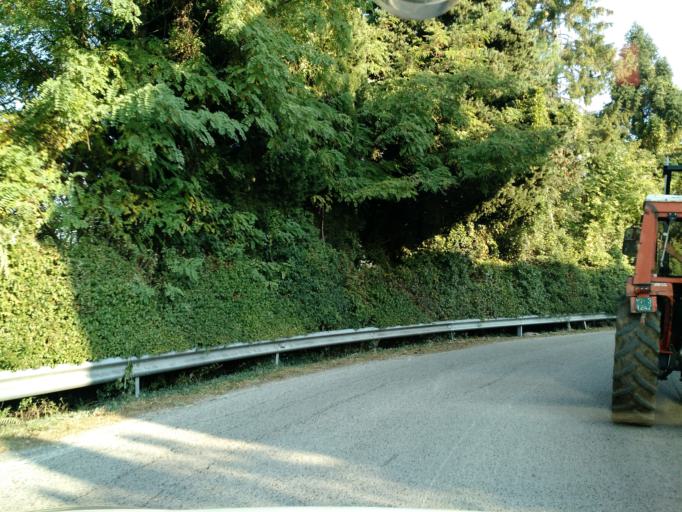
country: IT
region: Veneto
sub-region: Provincia di Vicenza
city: Salcedo
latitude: 45.7604
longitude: 11.5661
